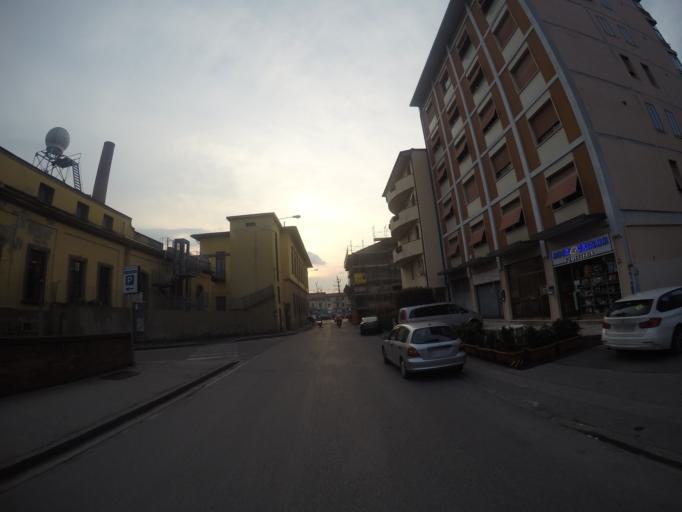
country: IT
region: Tuscany
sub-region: Provincia di Prato
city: Prato
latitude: 43.8857
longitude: 11.0995
